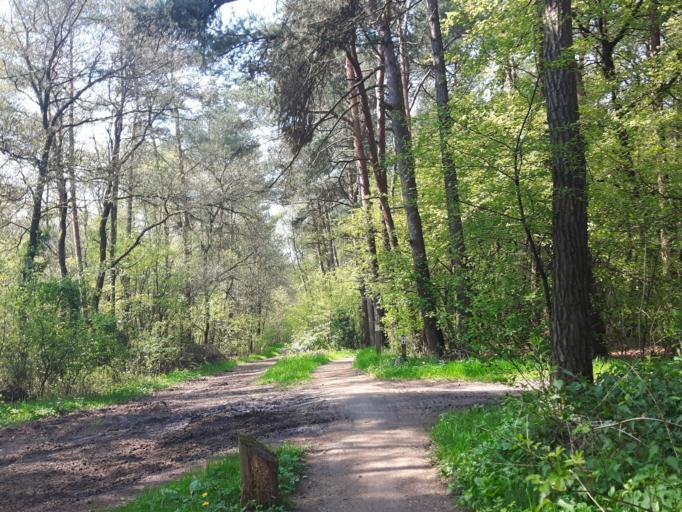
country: DE
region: North Rhine-Westphalia
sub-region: Regierungsbezirk Munster
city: Vreden
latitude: 52.1186
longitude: 6.8131
